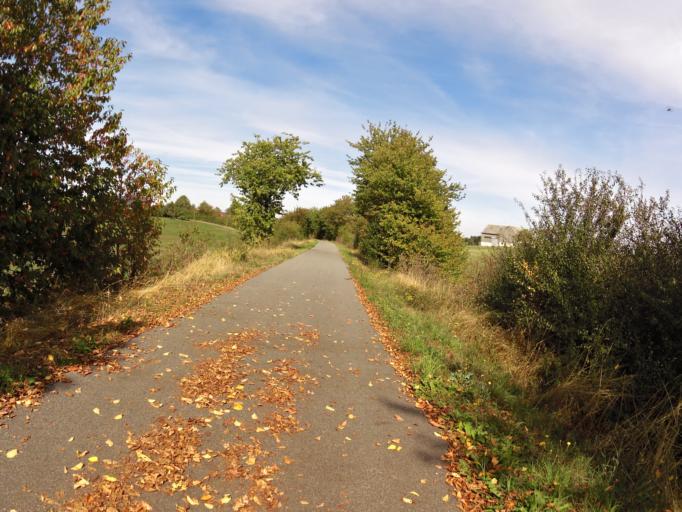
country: DE
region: Rheinland-Pfalz
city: Lichtenborn
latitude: 50.1185
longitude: 6.2673
